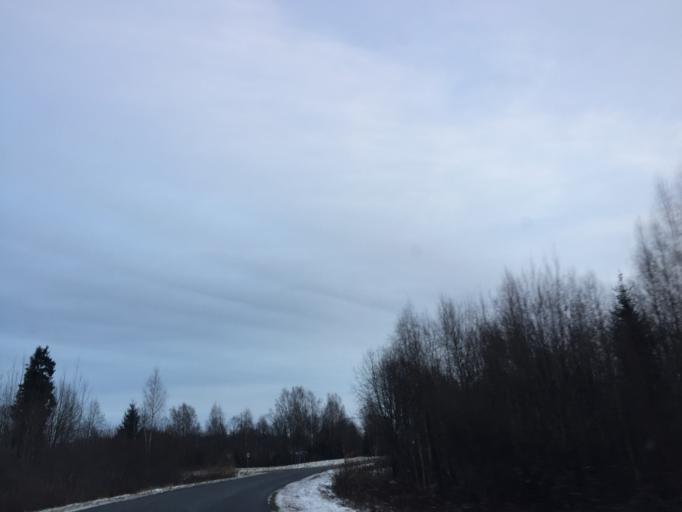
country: LV
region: Aloja
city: Aloja
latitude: 57.6500
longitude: 24.9919
